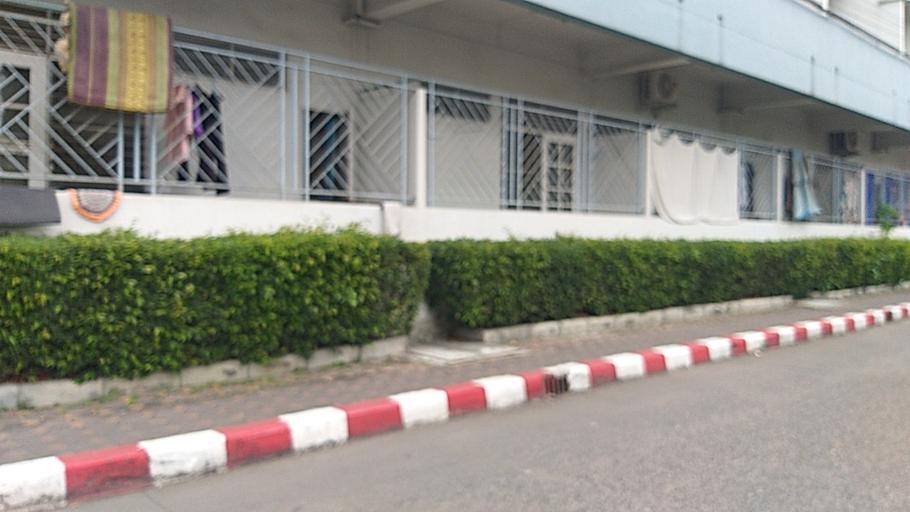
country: TH
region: Bangkok
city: Bang Na
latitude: 13.6700
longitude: 100.6814
